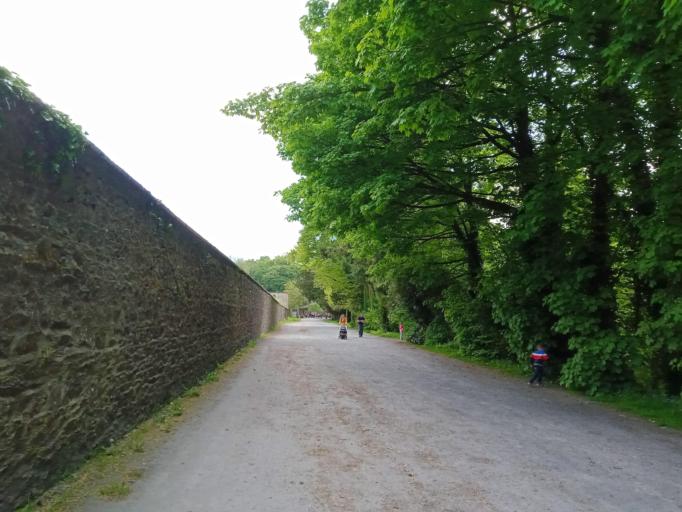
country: IE
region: Leinster
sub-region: Kilkenny
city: Castlecomer
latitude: 52.8087
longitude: -7.2035
